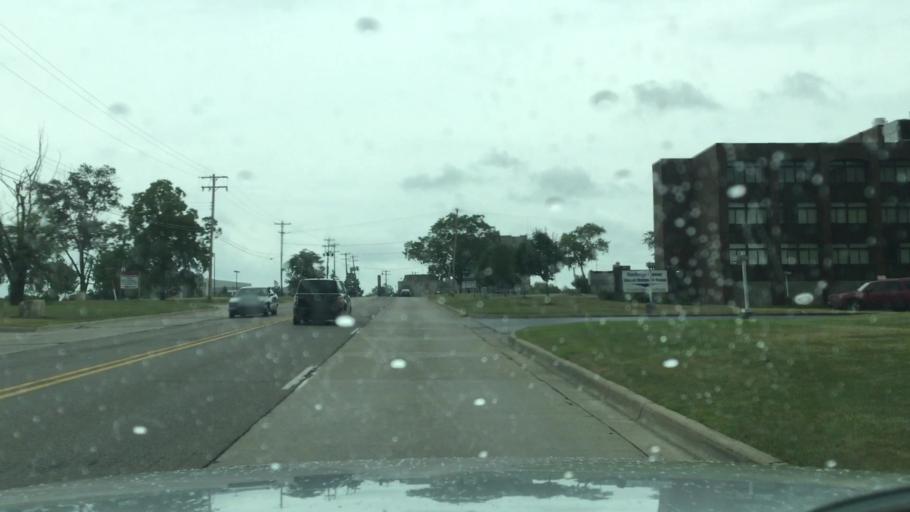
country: US
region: Michigan
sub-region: Genesee County
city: Flint
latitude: 43.0153
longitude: -83.7398
